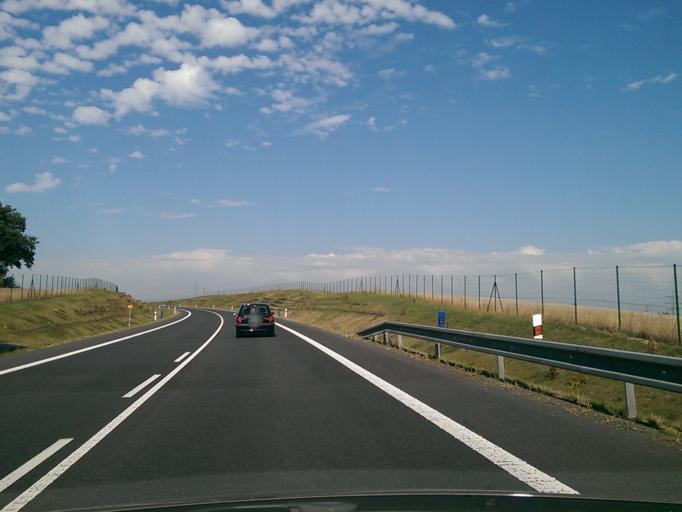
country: CZ
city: Hradek nad Nisou
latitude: 50.8526
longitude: 14.8907
